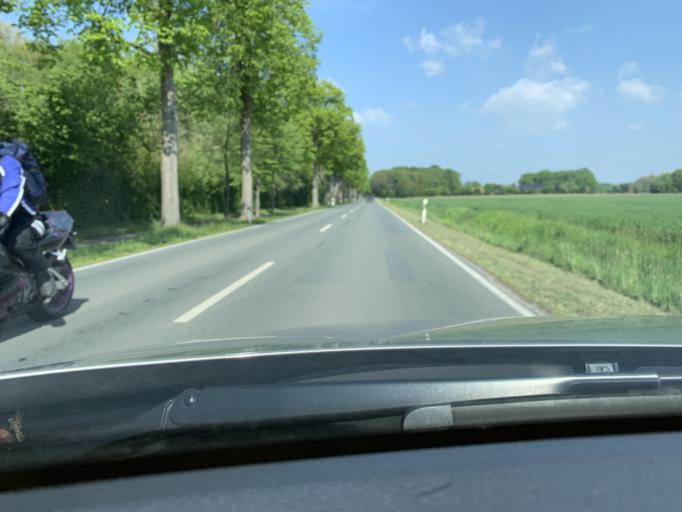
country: DE
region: North Rhine-Westphalia
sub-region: Regierungsbezirk Detmold
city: Langenberg
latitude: 51.7808
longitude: 8.3569
